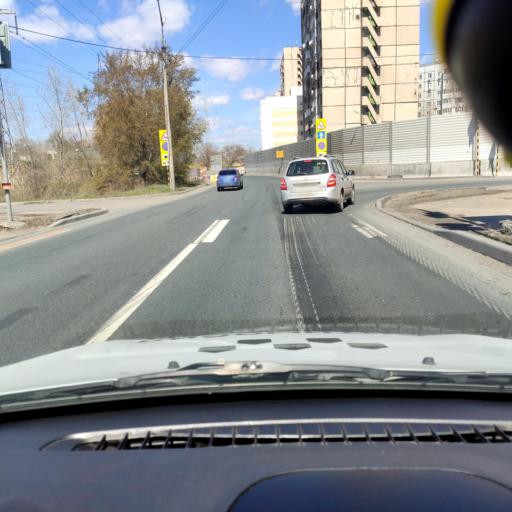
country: RU
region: Samara
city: Zhigulevsk
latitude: 53.4708
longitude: 49.5128
